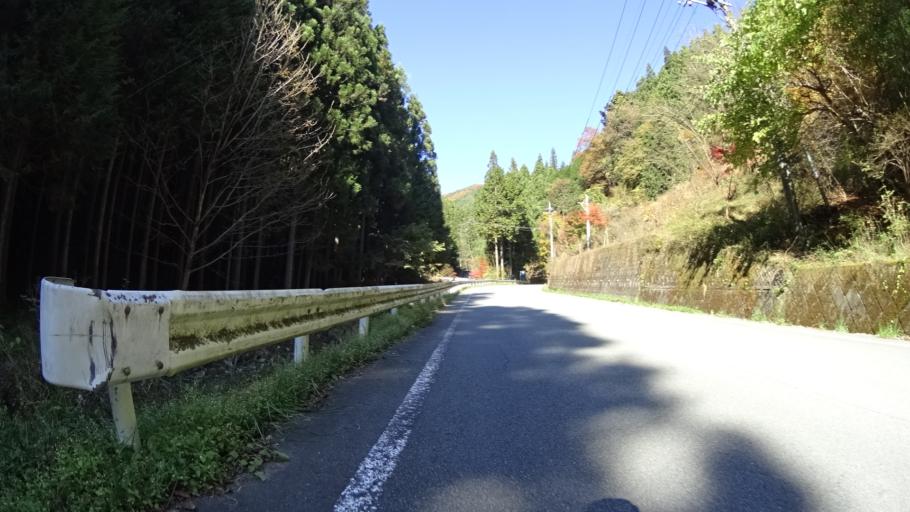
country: JP
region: Yamanashi
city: Otsuki
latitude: 35.7655
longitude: 138.9360
